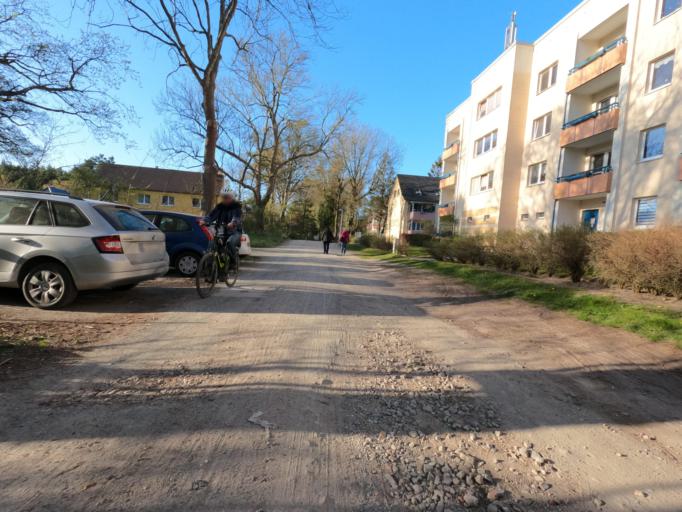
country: DE
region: Mecklenburg-Vorpommern
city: Ostseebad Prerow
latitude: 54.4443
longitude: 12.5521
